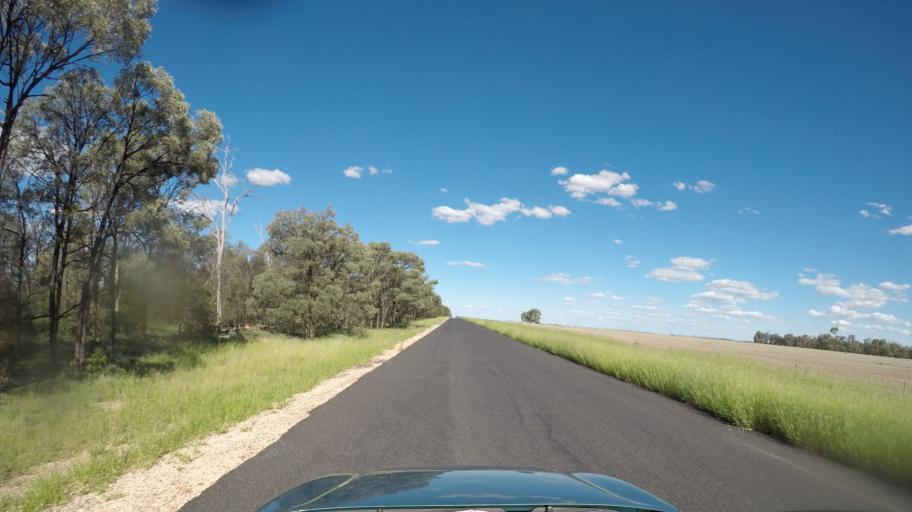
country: AU
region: Queensland
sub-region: Goondiwindi
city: Goondiwindi
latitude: -28.1585
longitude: 150.3919
